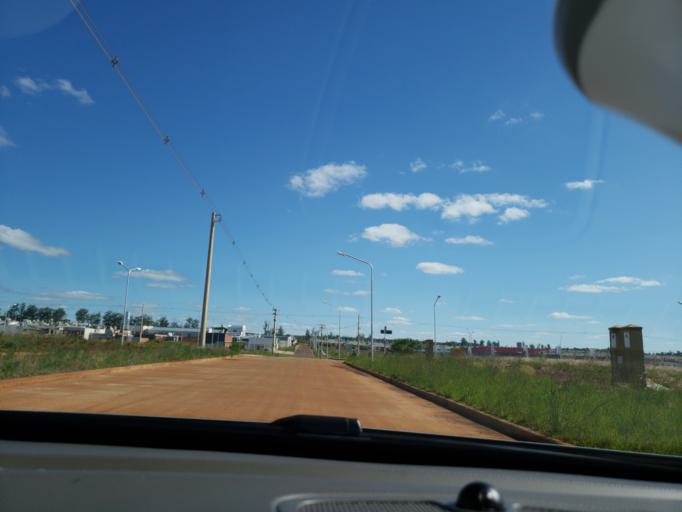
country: AR
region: Misiones
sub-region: Departamento de Capital
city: Posadas
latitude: -27.4068
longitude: -55.9839
